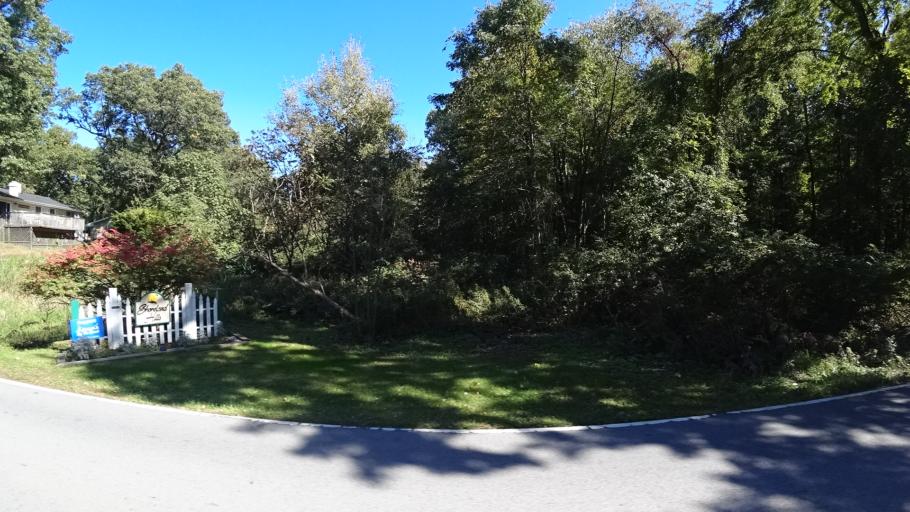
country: US
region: Indiana
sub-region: LaPorte County
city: Long Beach
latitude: 41.7493
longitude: -86.8316
